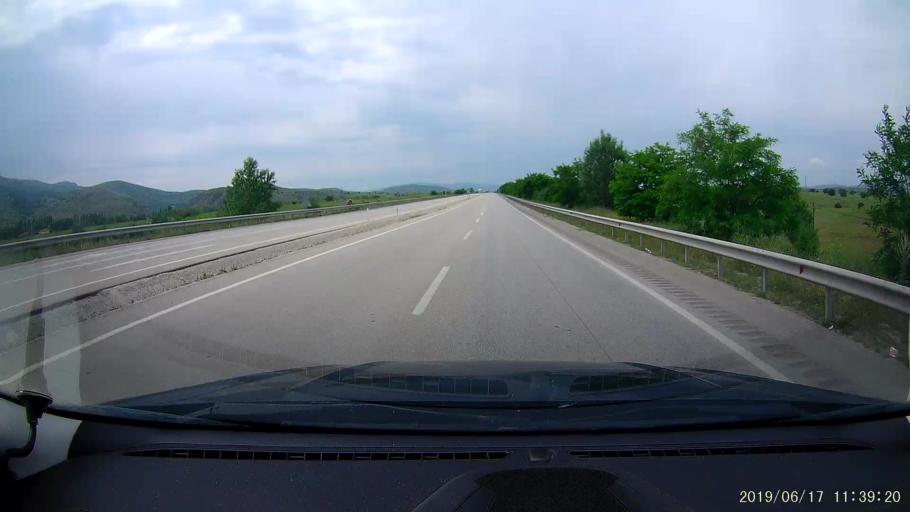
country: TR
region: Cankiri
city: Kursunlu
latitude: 40.8413
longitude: 33.3779
